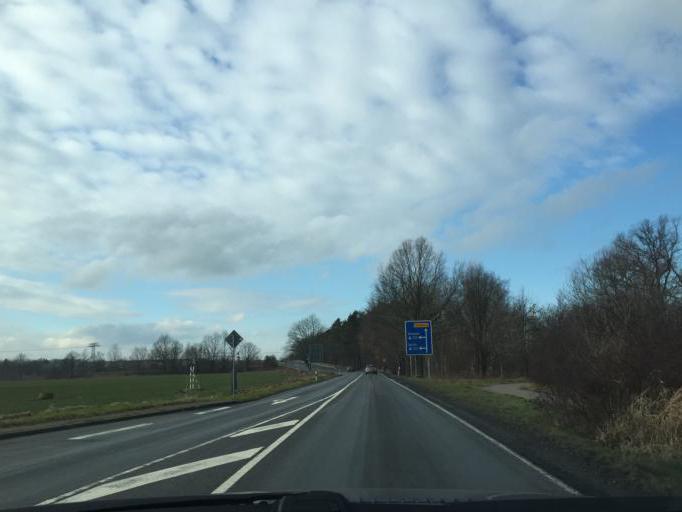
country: DE
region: Saxony
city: Radeburg
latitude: 51.2116
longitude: 13.7427
